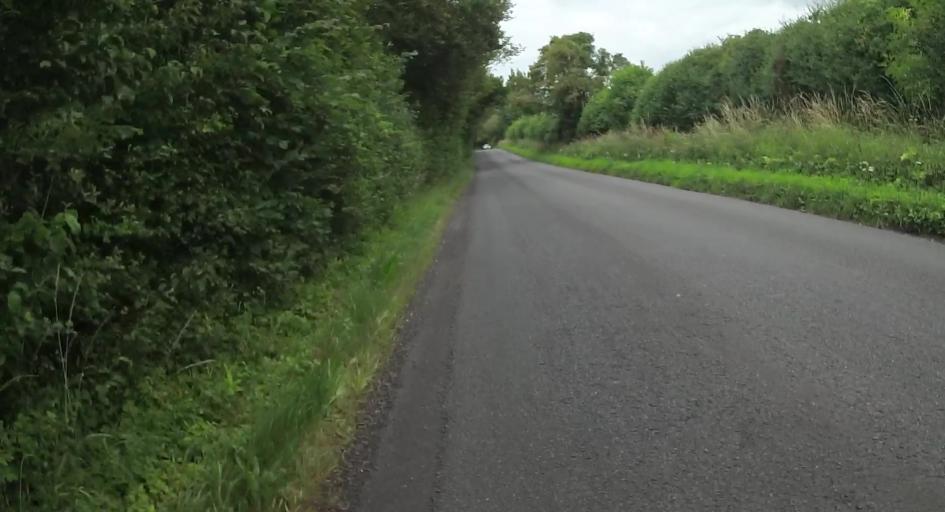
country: GB
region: England
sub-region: Hampshire
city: Bishops Waltham
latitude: 51.0218
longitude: -1.2010
